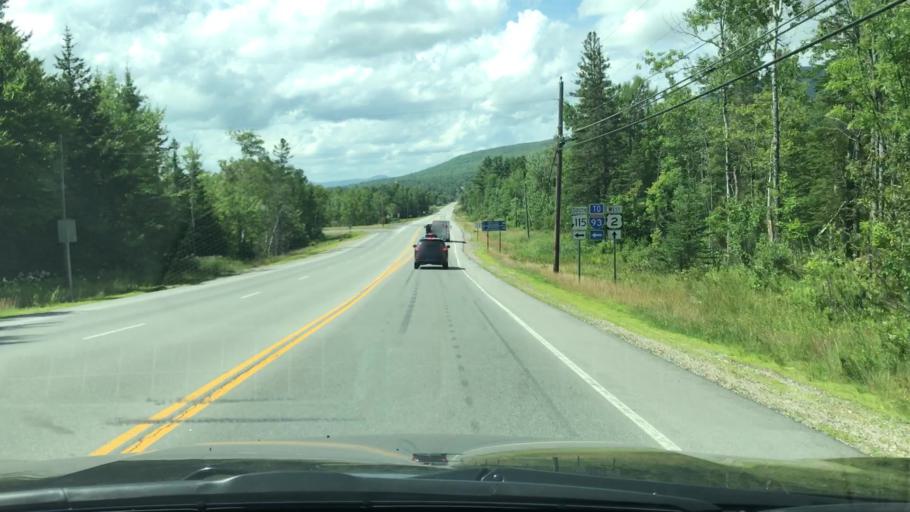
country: US
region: New Hampshire
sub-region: Coos County
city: Jefferson
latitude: 44.3796
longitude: -71.4157
